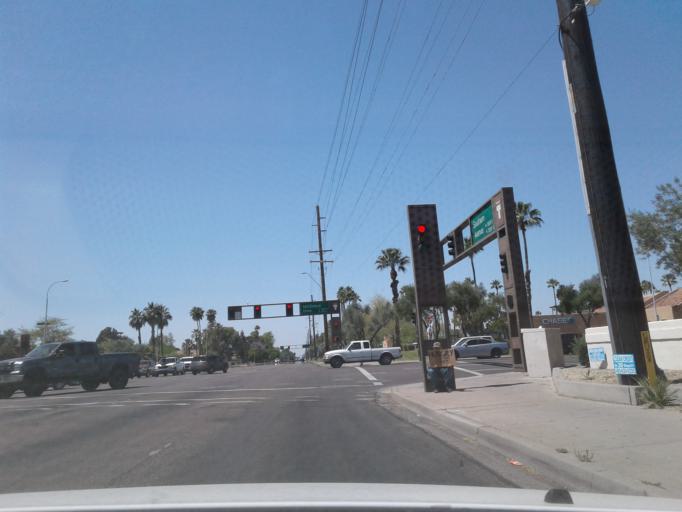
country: US
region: Arizona
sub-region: Maricopa County
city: Tempe
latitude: 33.3930
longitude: -111.9087
